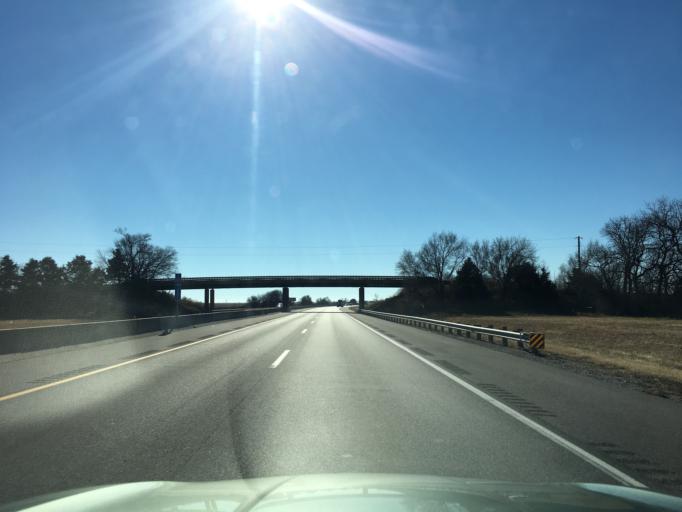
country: US
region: Kansas
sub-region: Sumner County
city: Wellington
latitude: 37.3203
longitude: -97.3397
